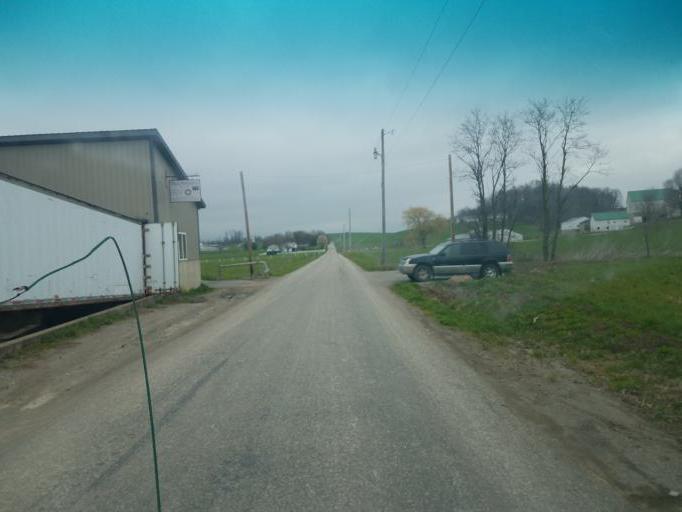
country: US
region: Ohio
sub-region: Tuscarawas County
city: Sugarcreek
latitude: 40.6114
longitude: -81.7313
